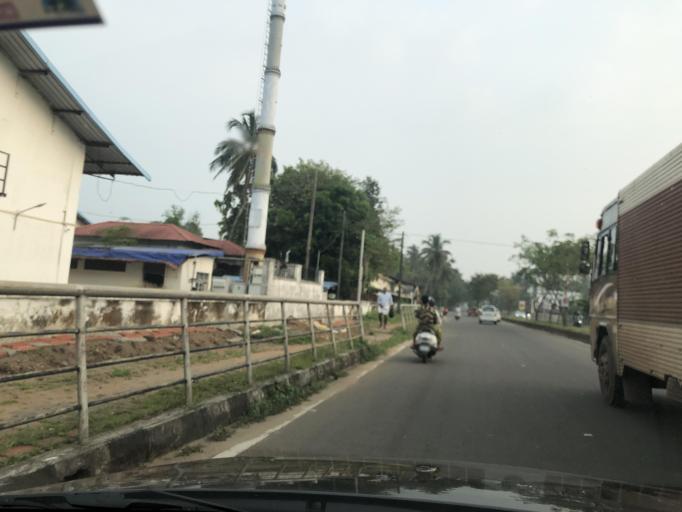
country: IN
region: Kerala
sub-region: Kozhikode
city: Kozhikode
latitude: 11.2836
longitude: 75.7611
